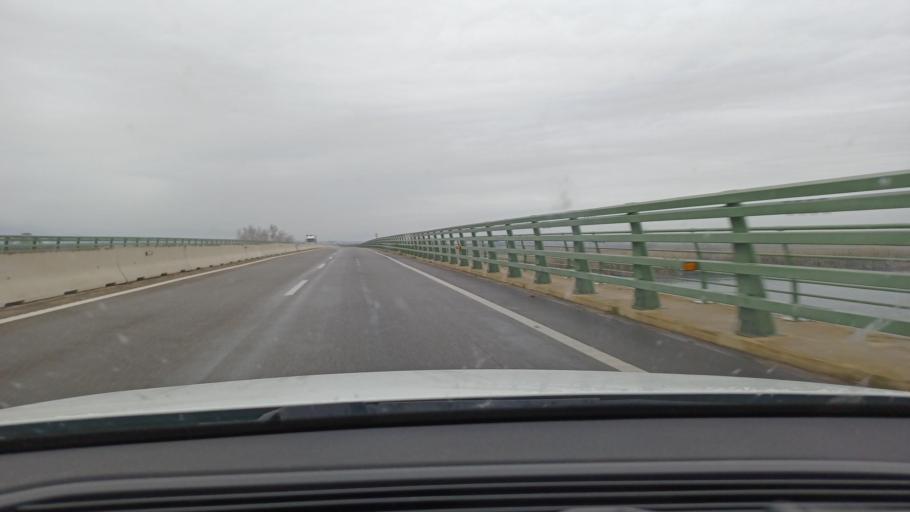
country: ES
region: Catalonia
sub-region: Provincia de Tarragona
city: Amposta
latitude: 40.7082
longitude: 0.5911
